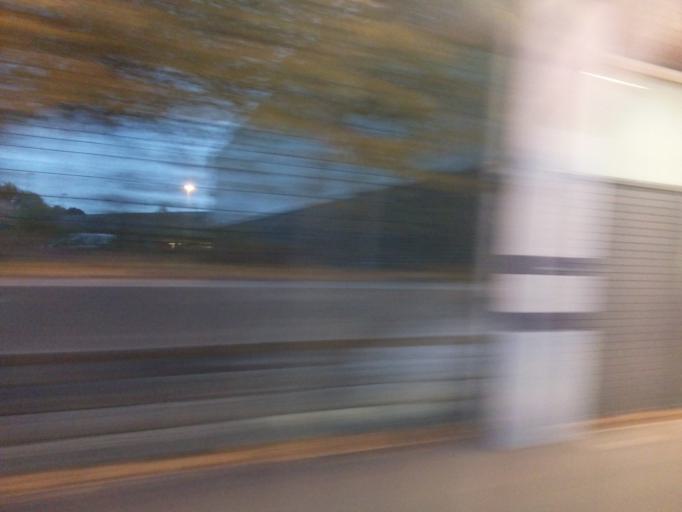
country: GB
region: England
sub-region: Rotherham
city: Rotherham
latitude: 53.4315
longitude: -1.3614
